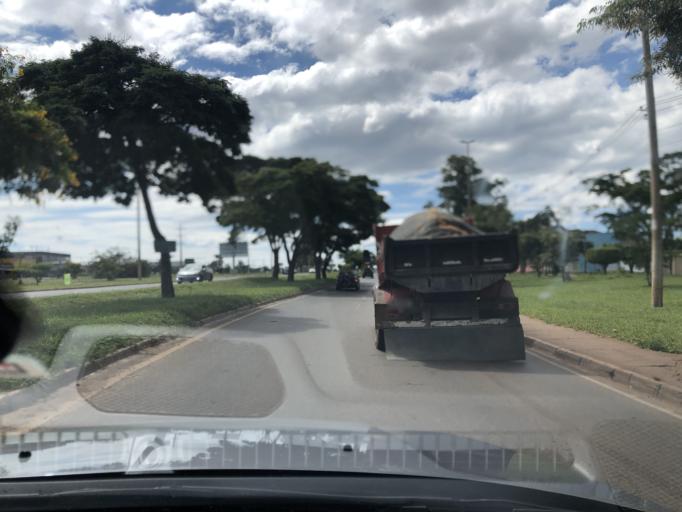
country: BR
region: Federal District
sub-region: Brasilia
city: Brasilia
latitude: -15.9975
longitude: -48.0580
